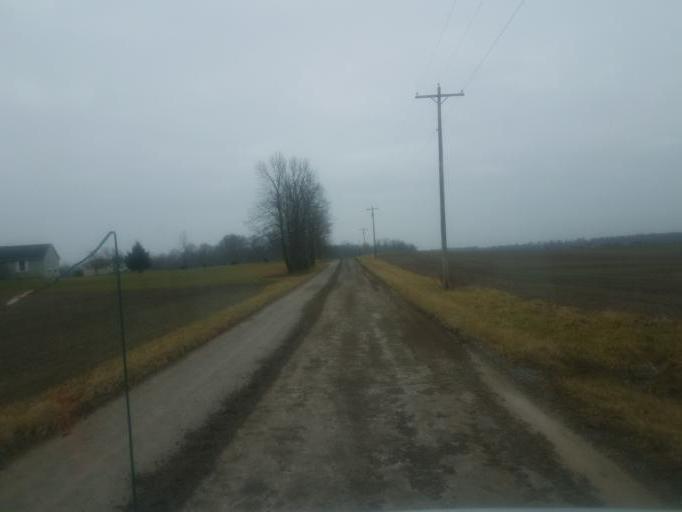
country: US
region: Ohio
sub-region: Knox County
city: Centerburg
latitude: 40.3856
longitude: -82.7421
